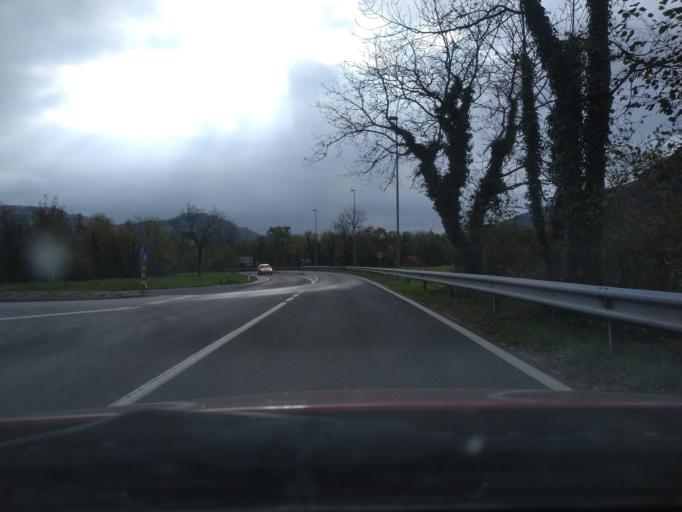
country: SI
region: Tolmin
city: Tolmin
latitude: 46.1856
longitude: 13.7080
